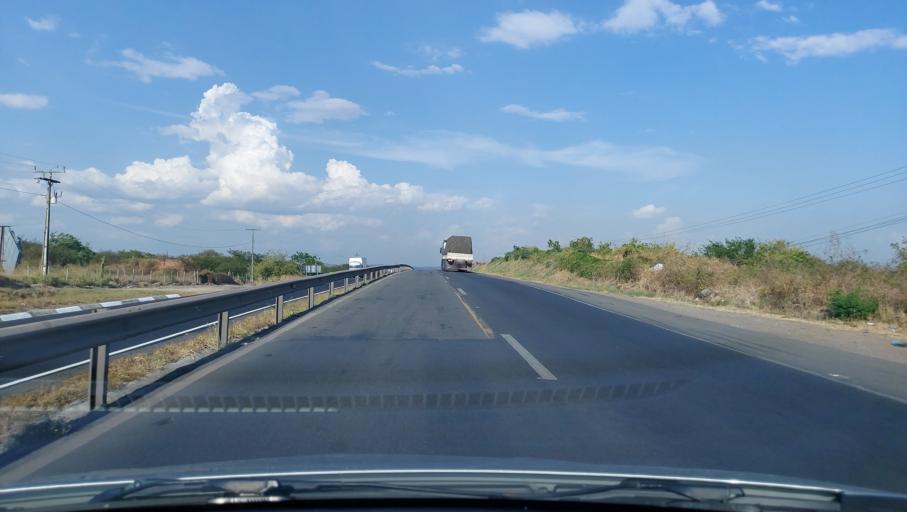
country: BR
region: Bahia
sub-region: Santo Estevao
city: Santo Estevao
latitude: -12.4269
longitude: -39.2083
